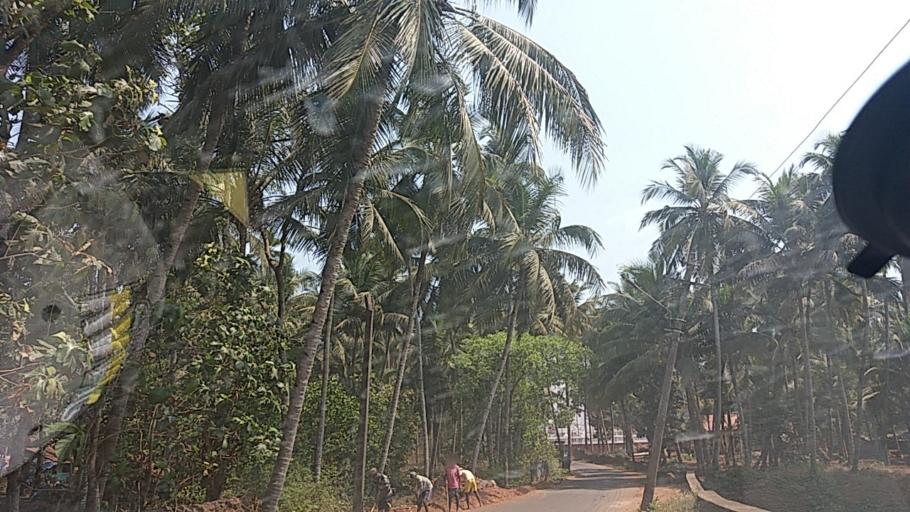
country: IN
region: Goa
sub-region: South Goa
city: Sancoale
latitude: 15.3728
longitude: 73.9147
